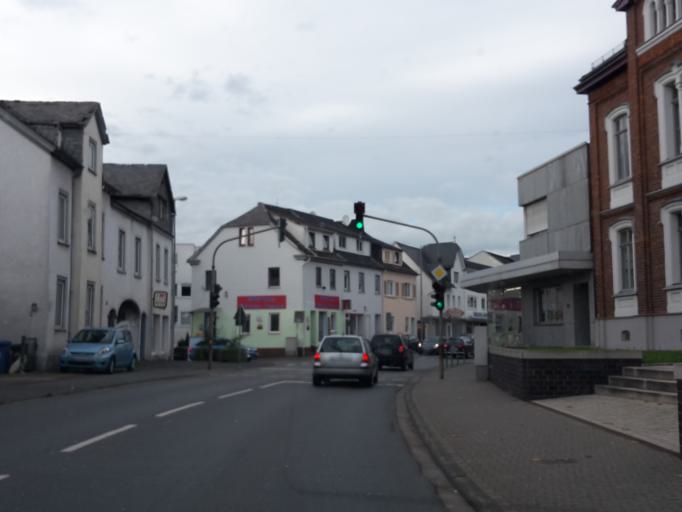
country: DE
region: Hesse
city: Bad Camberg
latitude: 50.2953
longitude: 8.2694
